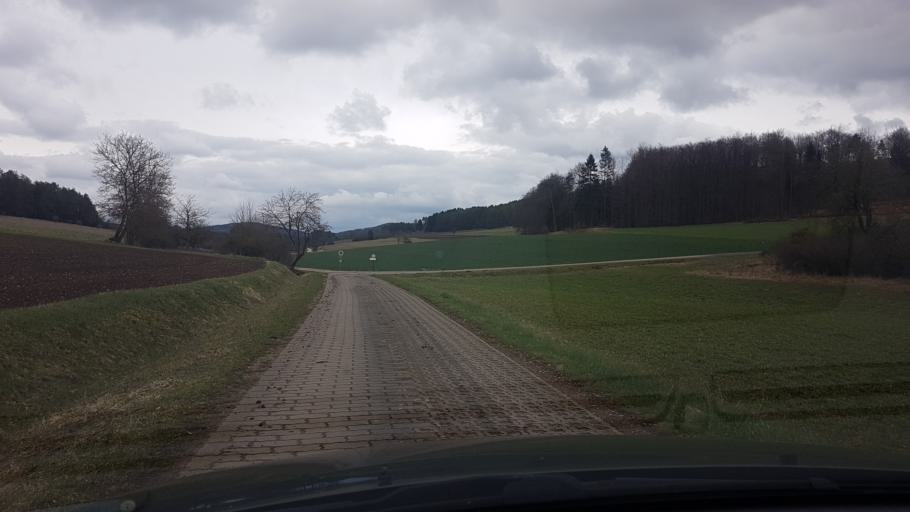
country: DE
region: Bavaria
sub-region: Upper Franconia
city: Poxdorf
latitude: 49.8861
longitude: 11.0837
